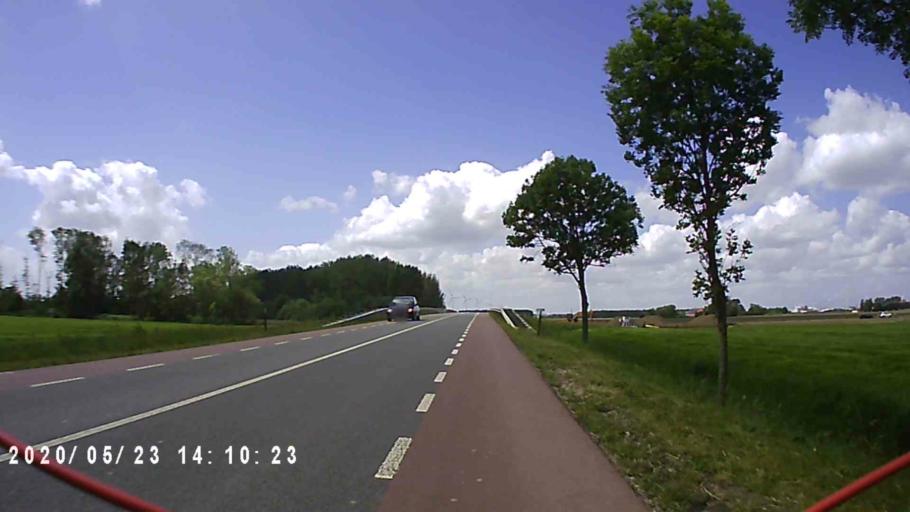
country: NL
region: Groningen
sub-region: Gemeente Delfzijl
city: Delfzijl
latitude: 53.2855
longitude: 7.0173
